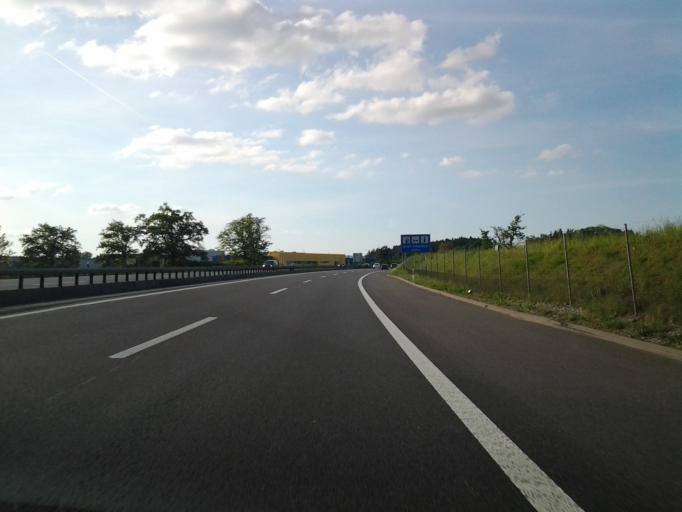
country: CH
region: Lucerne
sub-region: Hochdorf District
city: Emmen
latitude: 47.0932
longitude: 8.2471
